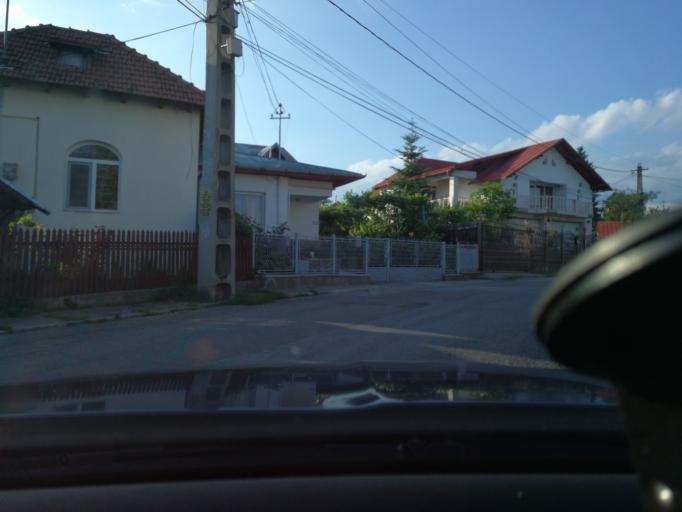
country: RO
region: Prahova
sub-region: Comuna Cornu
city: Cornu de Jos
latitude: 45.1470
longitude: 25.7106
